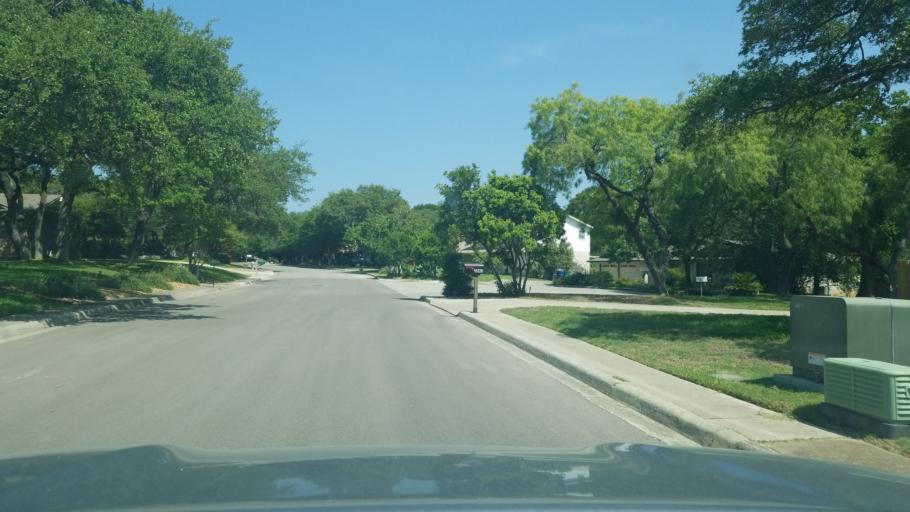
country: US
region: Texas
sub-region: Bexar County
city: Hollywood Park
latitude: 29.5880
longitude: -98.4595
